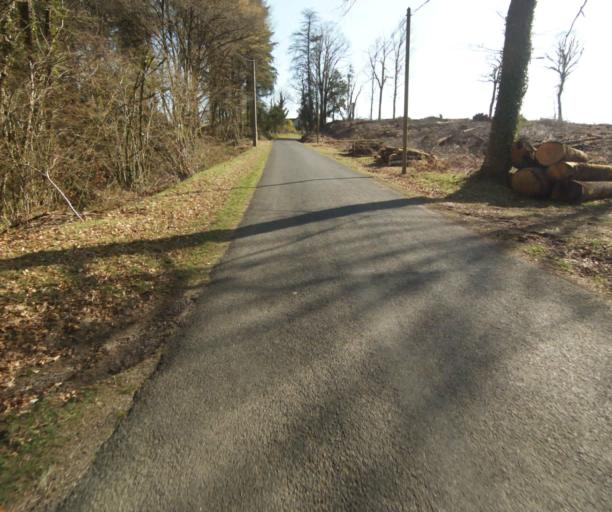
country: FR
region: Limousin
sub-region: Departement de la Correze
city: Saint-Mexant
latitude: 45.3227
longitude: 1.6251
